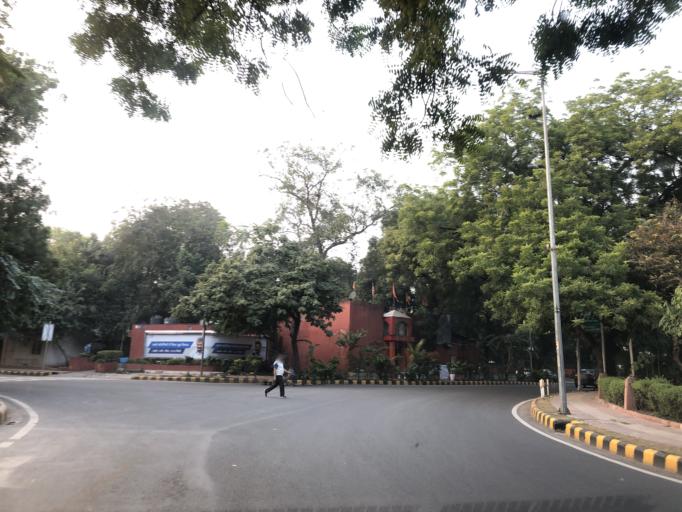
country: IN
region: NCT
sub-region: New Delhi
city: New Delhi
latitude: 28.6202
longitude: 77.2061
